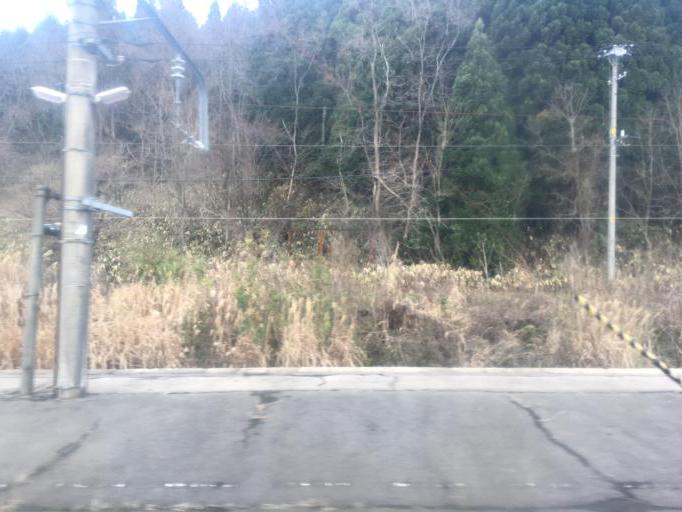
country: JP
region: Akita
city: Takanosu
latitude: 40.2127
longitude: 140.2357
